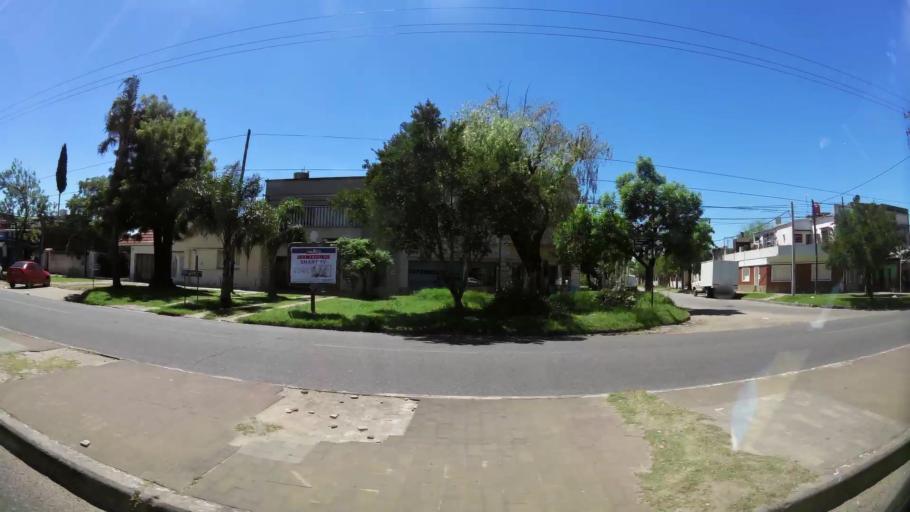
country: AR
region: Santa Fe
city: Santa Fe de la Vera Cruz
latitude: -31.6208
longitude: -60.7135
